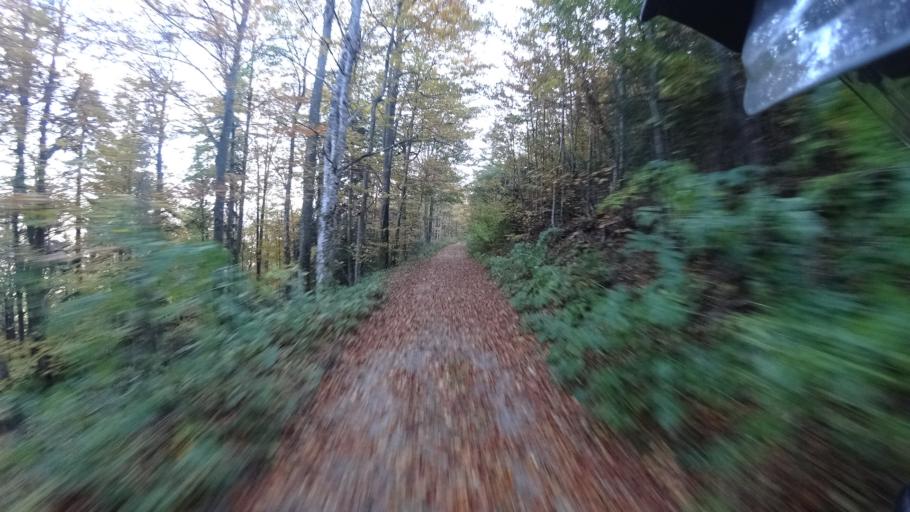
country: HR
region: Karlovacka
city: Plaski
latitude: 45.0158
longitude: 15.3829
